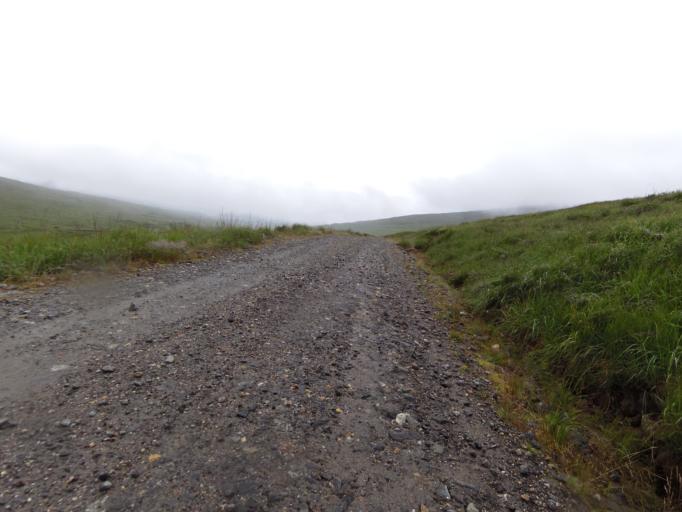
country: GB
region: Scotland
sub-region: Highland
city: Spean Bridge
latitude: 56.7711
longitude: -4.6998
